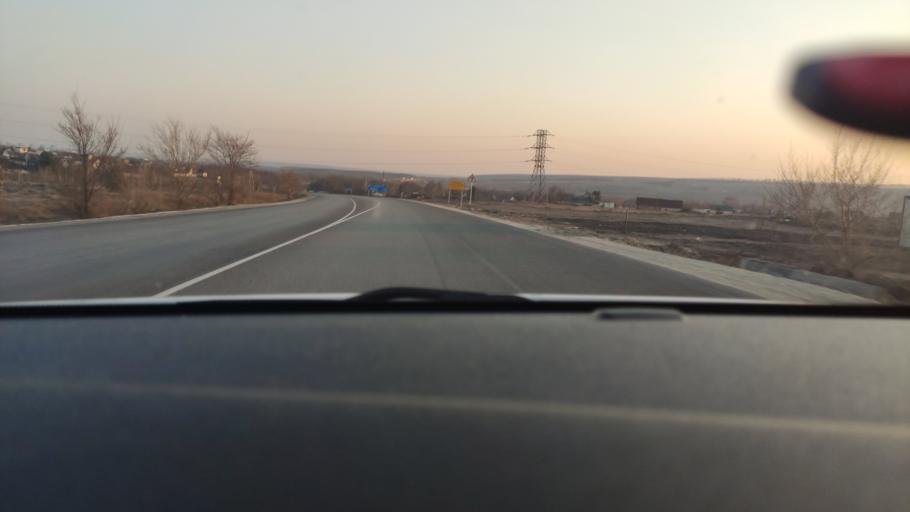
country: RU
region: Voronezj
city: Kolodeznyy
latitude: 51.3523
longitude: 39.1739
